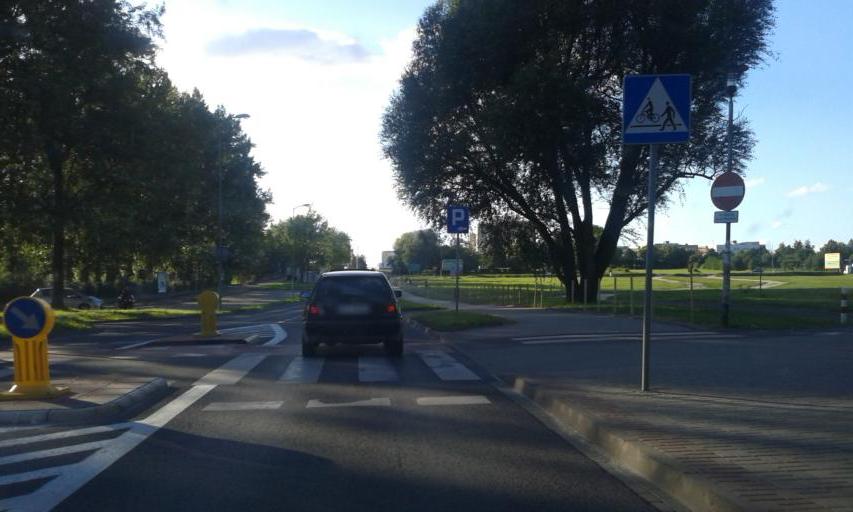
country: PL
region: West Pomeranian Voivodeship
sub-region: Koszalin
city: Koszalin
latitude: 54.1985
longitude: 16.2023
